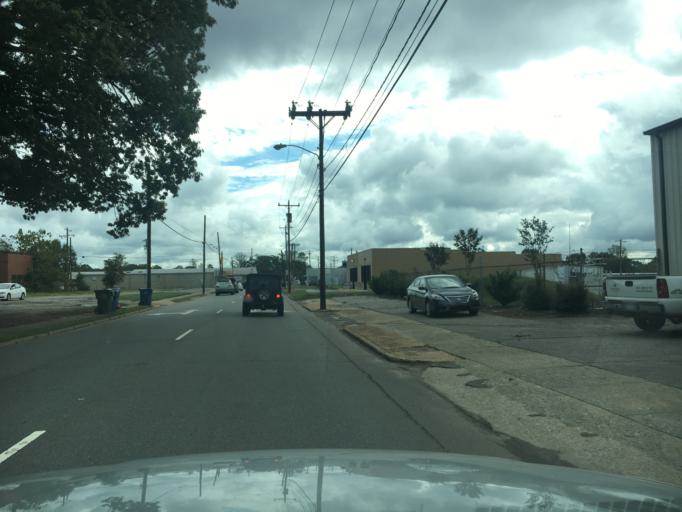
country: US
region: North Carolina
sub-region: Catawba County
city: Hickory
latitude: 35.7397
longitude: -81.3162
